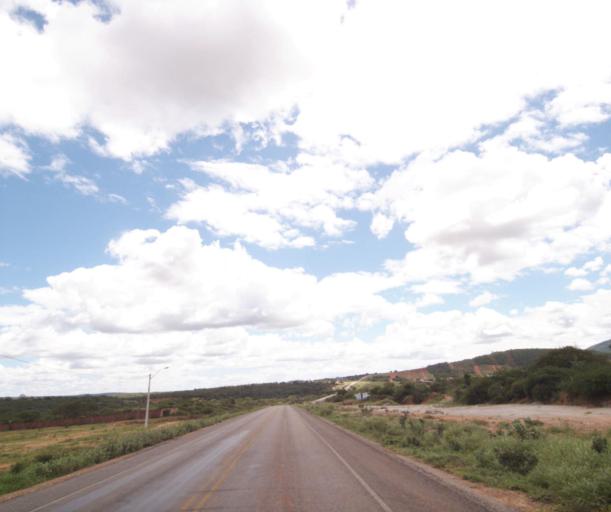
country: BR
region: Bahia
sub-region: Brumado
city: Brumado
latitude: -14.2282
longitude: -41.6765
